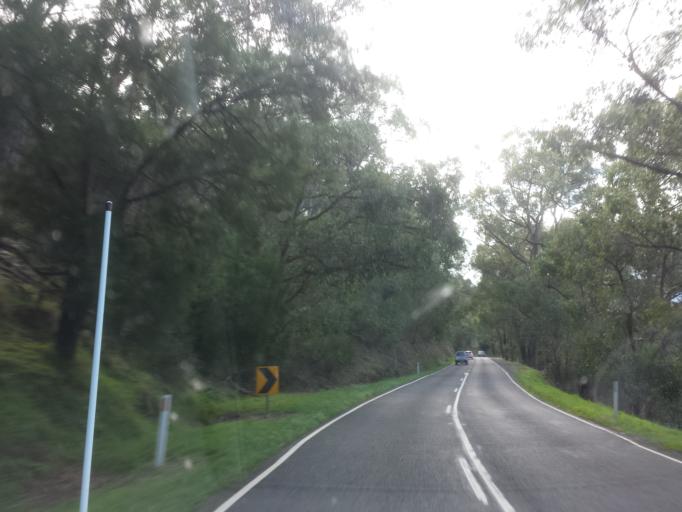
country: AU
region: Victoria
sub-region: Yarra Ranges
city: Yarra Glen
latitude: -37.6478
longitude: 145.3516
